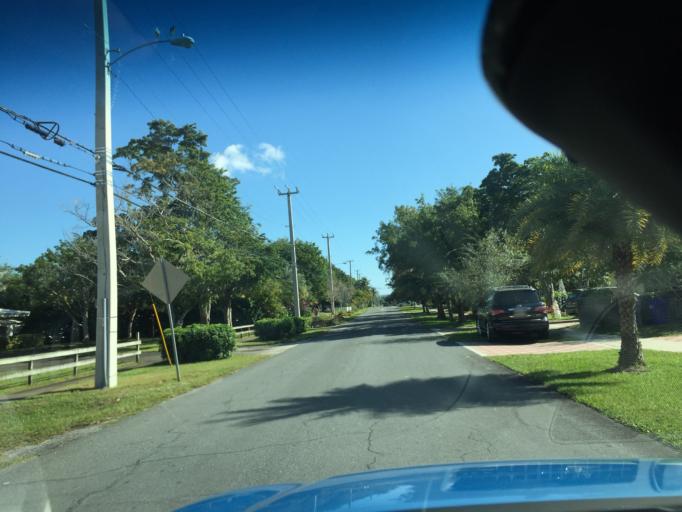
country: US
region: Florida
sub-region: Broward County
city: Pompano Beach
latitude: 26.2370
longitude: -80.1182
